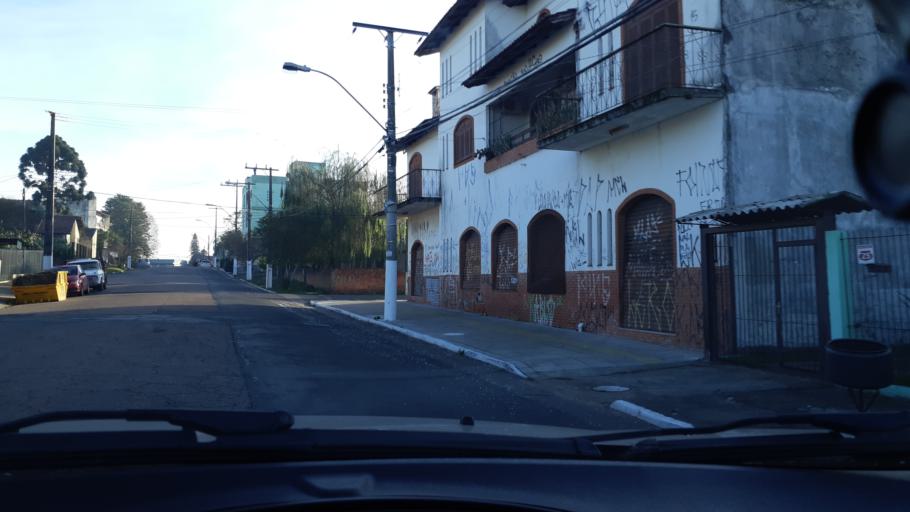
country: BR
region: Rio Grande do Sul
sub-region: Sapucaia Do Sul
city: Sapucaia
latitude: -29.8466
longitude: -51.1526
